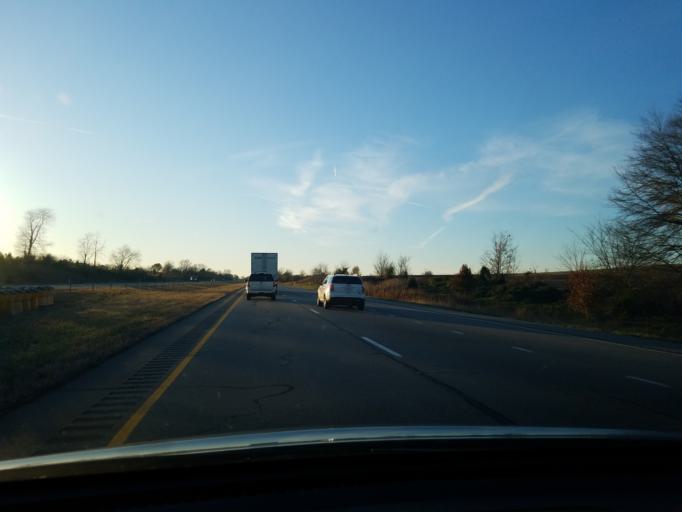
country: US
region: Indiana
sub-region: Gibson County
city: Haubstadt
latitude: 38.1697
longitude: -87.4767
